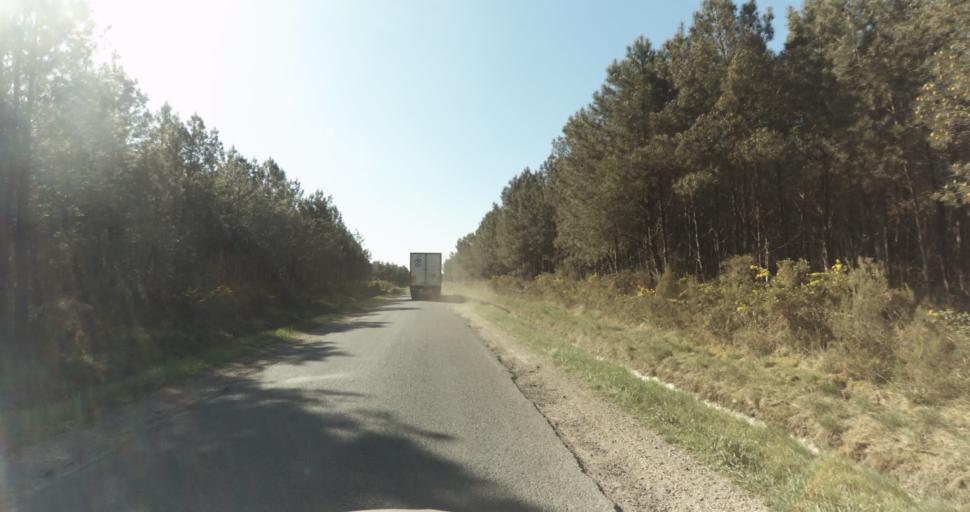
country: FR
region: Aquitaine
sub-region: Departement de la Gironde
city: Marcheprime
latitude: 44.7547
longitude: -0.8499
